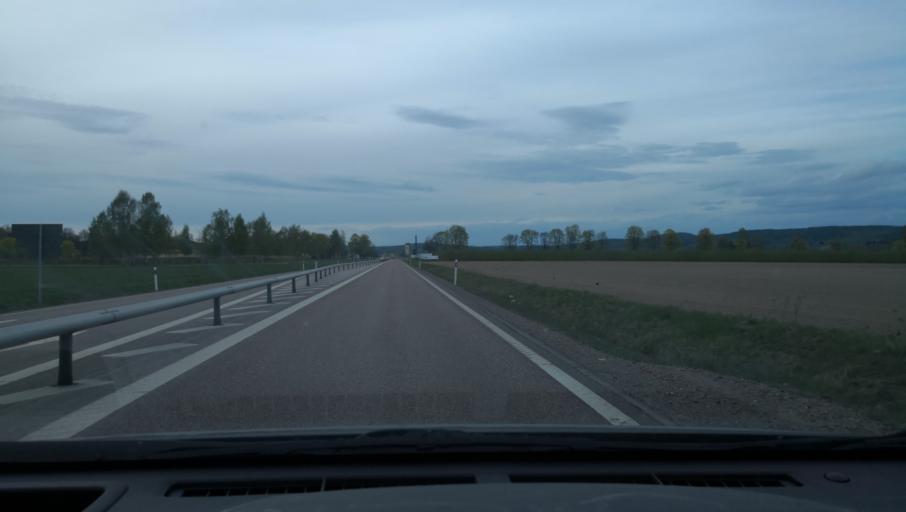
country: SE
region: Dalarna
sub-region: Hedemora Kommun
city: Brunna
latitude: 60.2730
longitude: 16.0016
